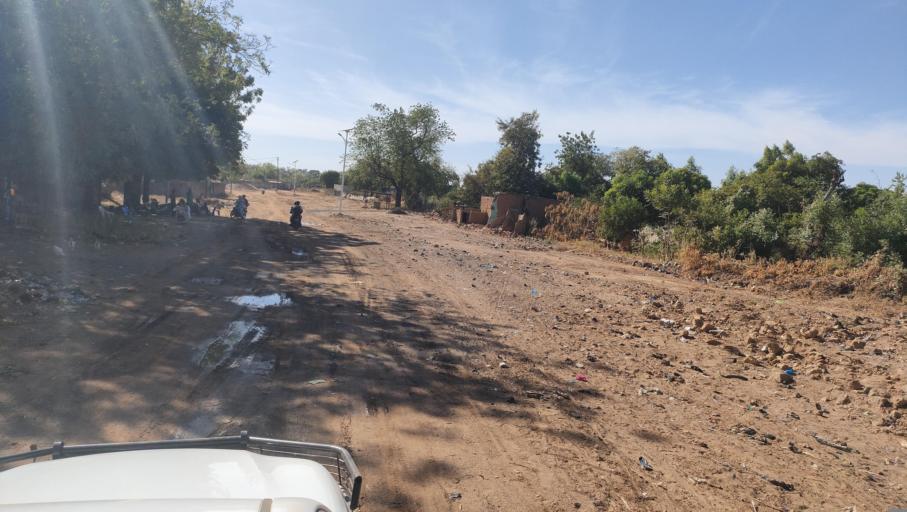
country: BF
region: Est
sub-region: Province du Gourma
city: Fada N'gourma
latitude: 12.0652
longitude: 0.3662
